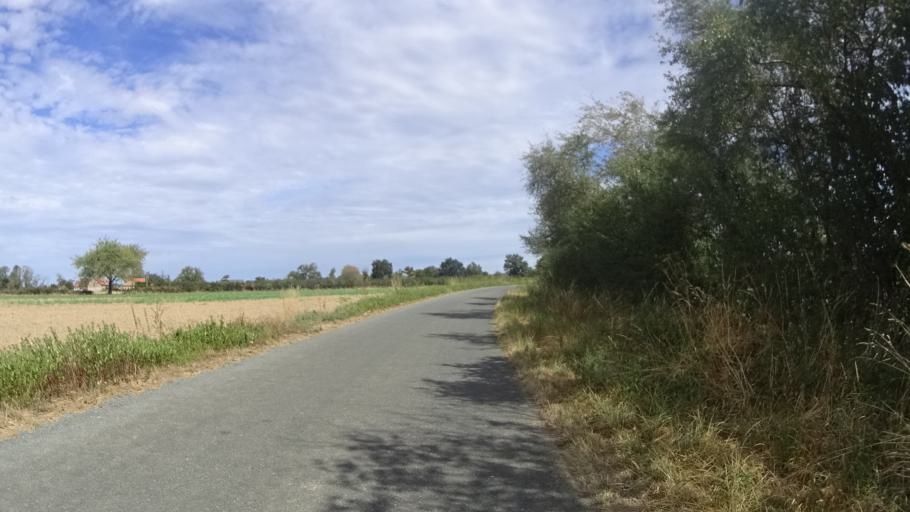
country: FR
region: Auvergne
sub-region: Departement de l'Allier
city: Beaulon
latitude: 46.6415
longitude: 3.6914
